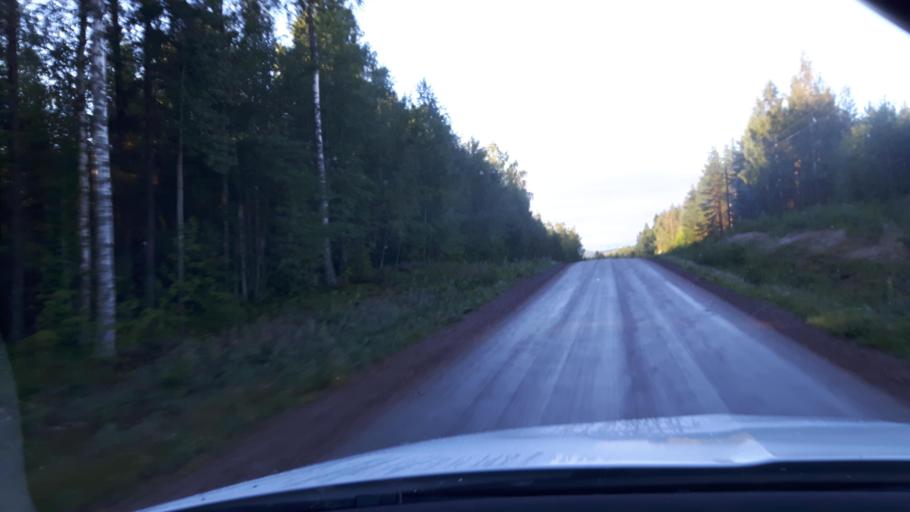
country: SE
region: Vaesternorrland
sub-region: Ange Kommun
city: Ange
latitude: 62.1619
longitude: 15.6593
